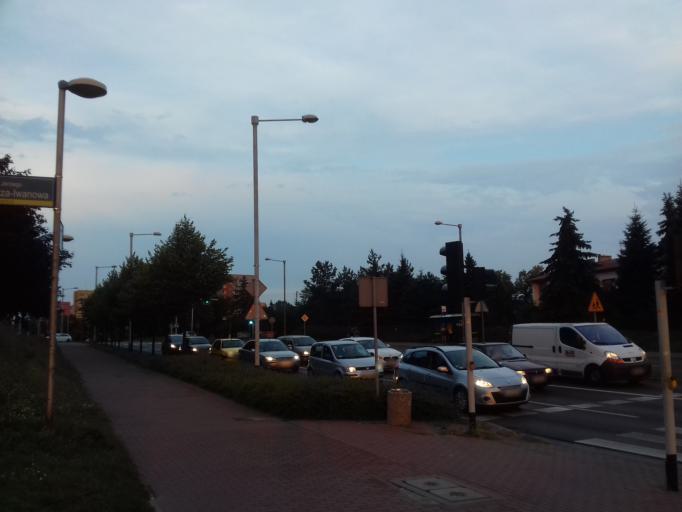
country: PL
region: Silesian Voivodeship
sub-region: Czestochowa
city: Czestochowa
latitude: 50.8243
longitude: 19.1053
